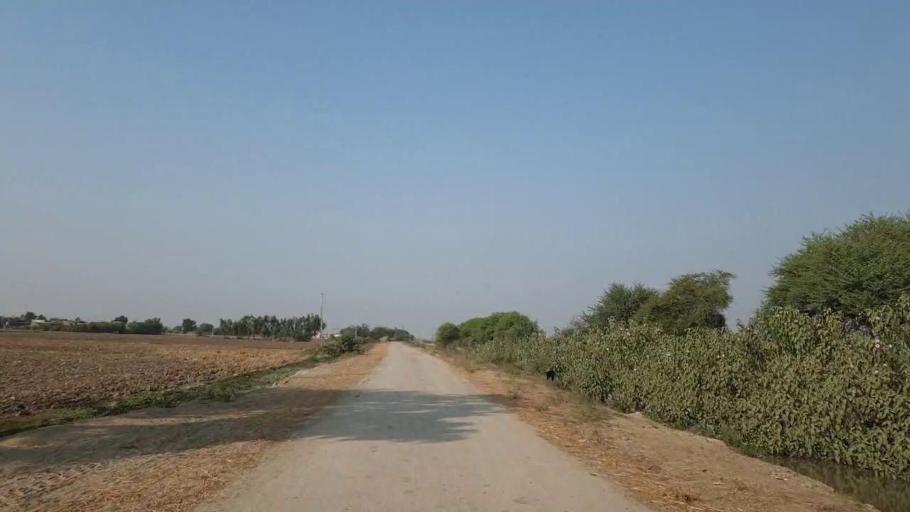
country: PK
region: Sindh
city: Bulri
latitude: 25.0001
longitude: 68.3774
